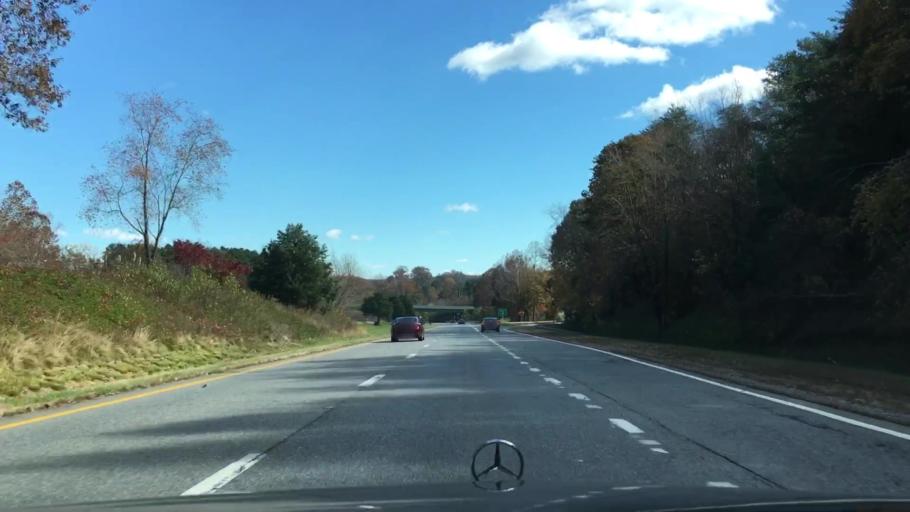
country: US
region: Virginia
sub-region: Campbell County
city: Altavista
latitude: 37.1385
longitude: -79.2543
